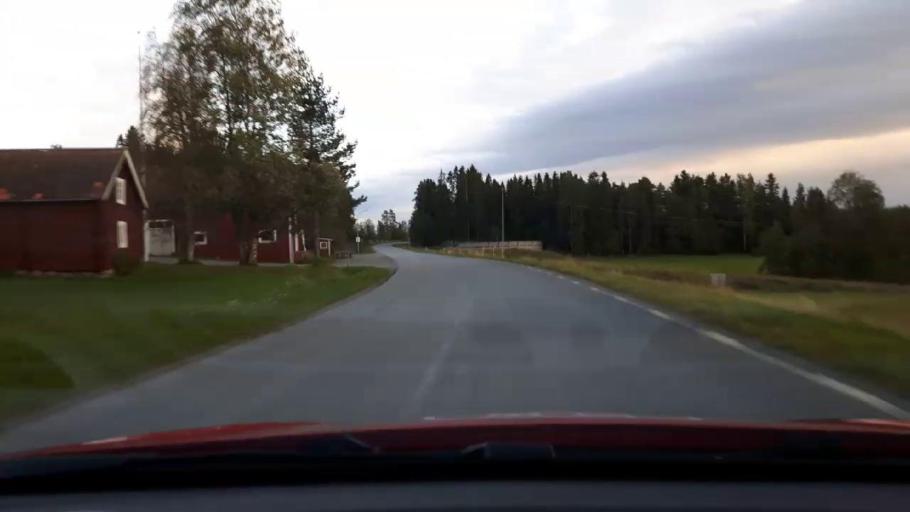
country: SE
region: Jaemtland
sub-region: OEstersunds Kommun
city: Ostersund
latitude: 63.0833
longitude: 14.4385
